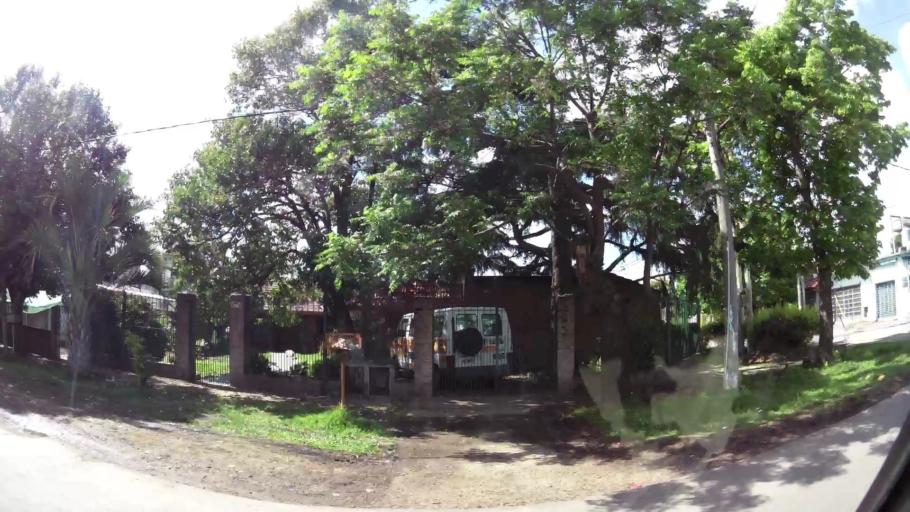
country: AR
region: Buenos Aires
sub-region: Partido de Quilmes
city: Quilmes
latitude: -34.8338
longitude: -58.1799
